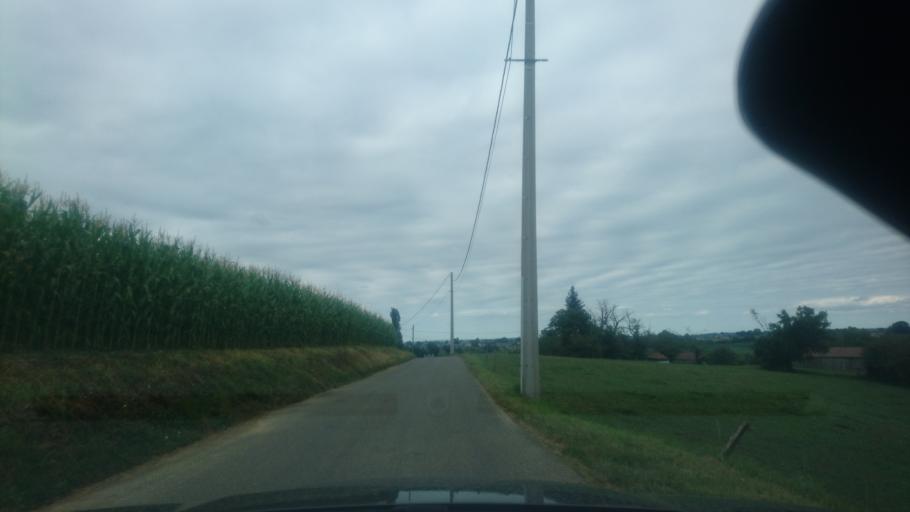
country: FR
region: Midi-Pyrenees
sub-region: Departement des Hautes-Pyrenees
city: Horgues
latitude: 43.1278
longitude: 0.0620
